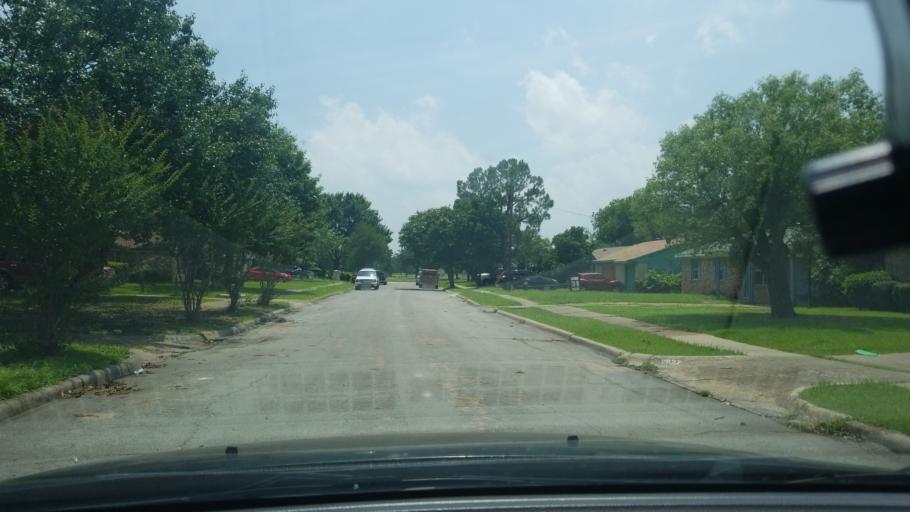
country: US
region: Texas
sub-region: Dallas County
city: Mesquite
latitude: 32.7986
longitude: -96.6422
